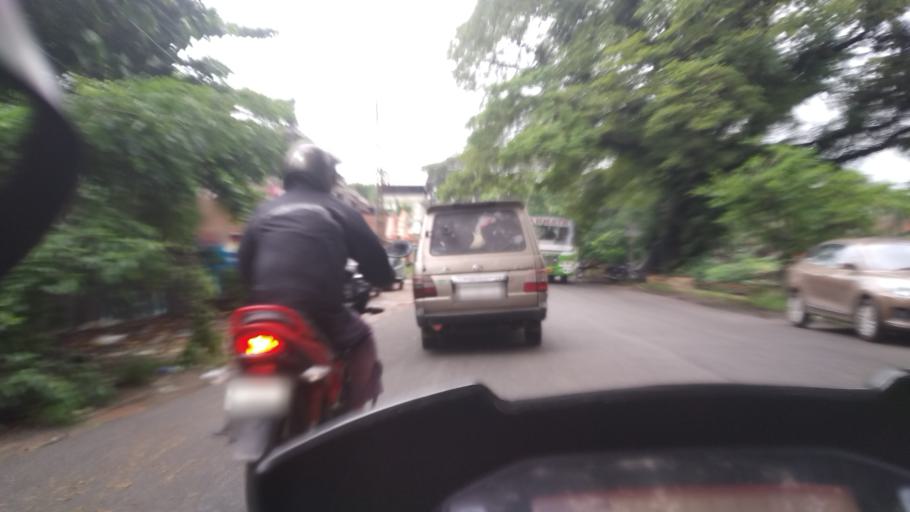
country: IN
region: Kerala
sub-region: Alappuzha
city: Alleppey
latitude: 9.5004
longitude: 76.3382
